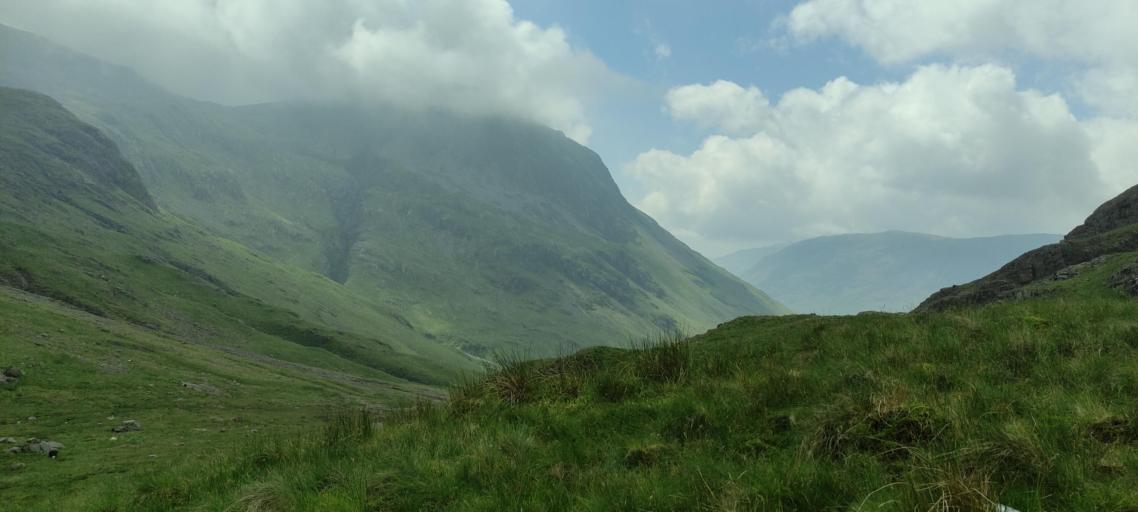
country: GB
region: England
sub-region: Cumbria
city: Keswick
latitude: 54.4739
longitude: -3.2022
